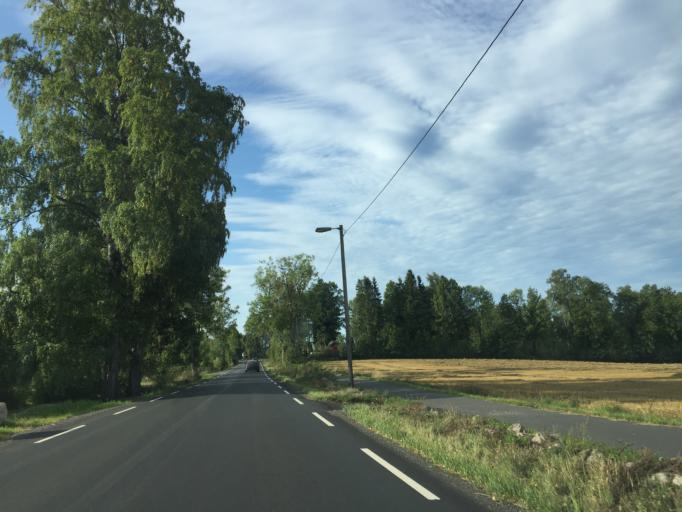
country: NO
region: Akershus
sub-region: As
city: As
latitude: 59.7123
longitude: 10.7730
